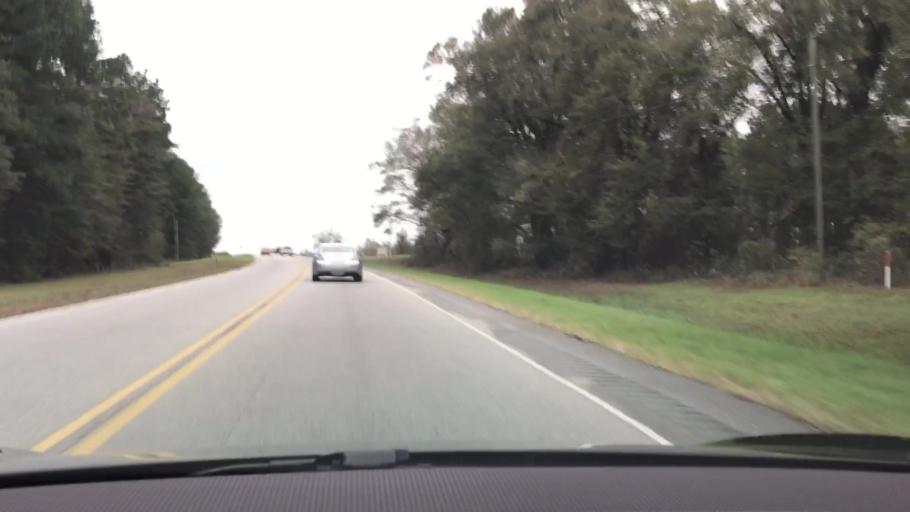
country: US
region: Georgia
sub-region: Jefferson County
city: Louisville
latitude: 32.9519
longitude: -82.3943
